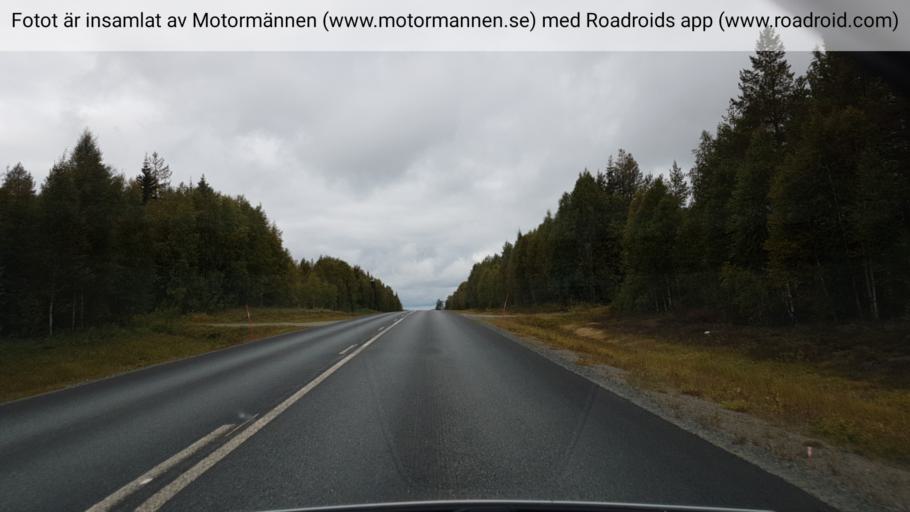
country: SE
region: Vaesterbotten
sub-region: Norsjo Kommun
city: Norsjoe
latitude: 64.9911
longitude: 19.3257
